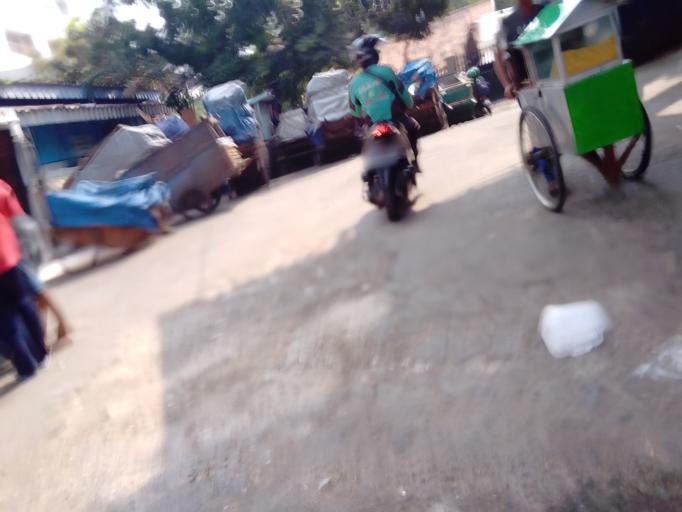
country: ID
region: Jakarta Raya
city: Jakarta
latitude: -6.2088
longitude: 106.7958
